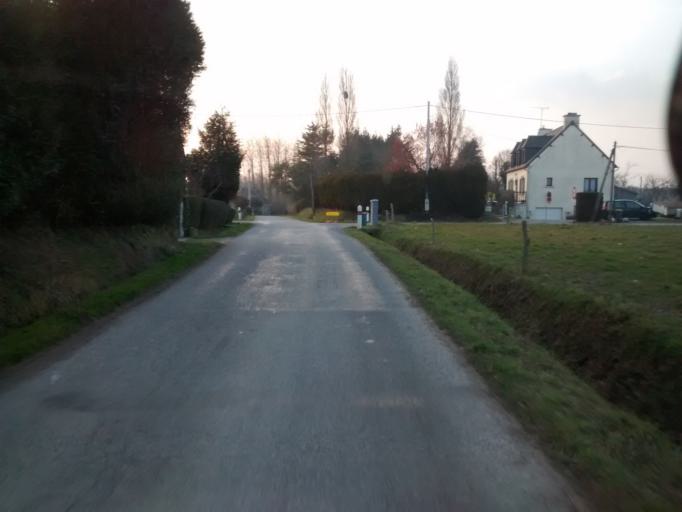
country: FR
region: Brittany
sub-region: Departement du Morbihan
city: Meneac
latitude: 48.1466
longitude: -2.4763
